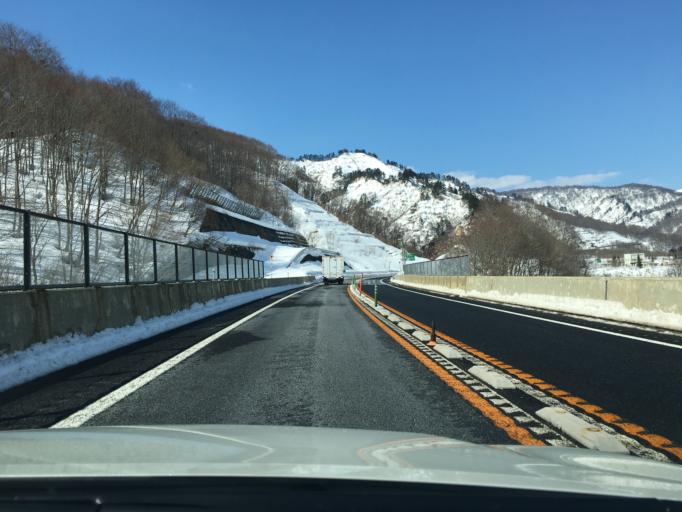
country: JP
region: Yamagata
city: Sagae
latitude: 38.4488
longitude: 139.9945
